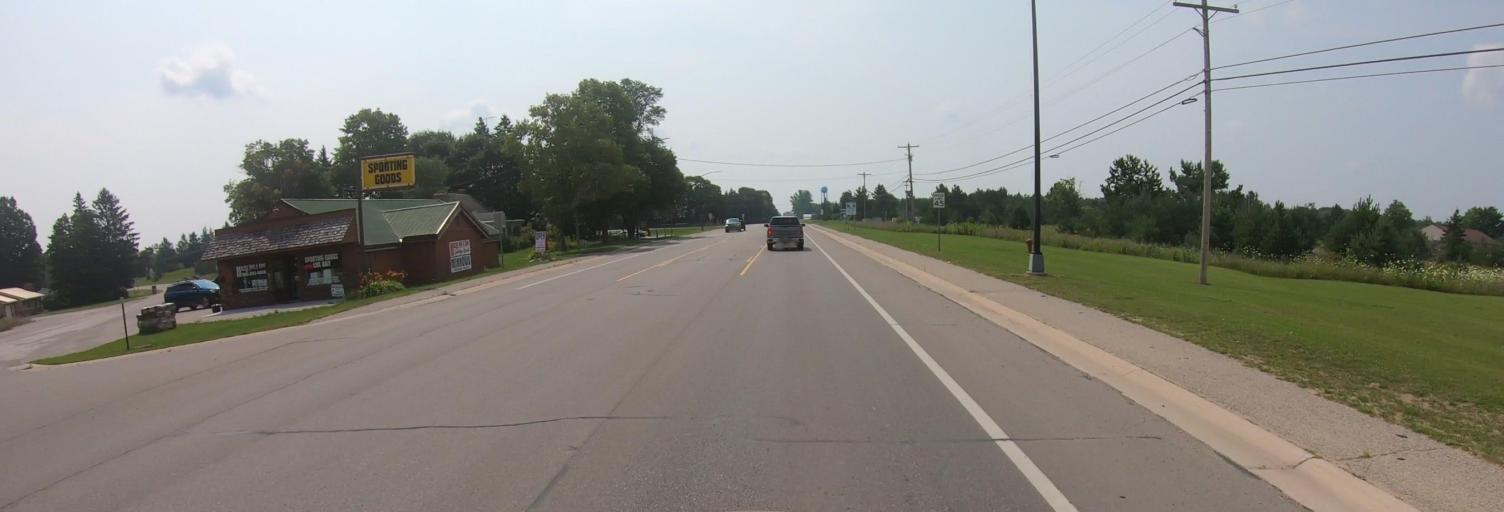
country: US
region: Michigan
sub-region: Luce County
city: Newberry
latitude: 46.3338
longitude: -85.5098
